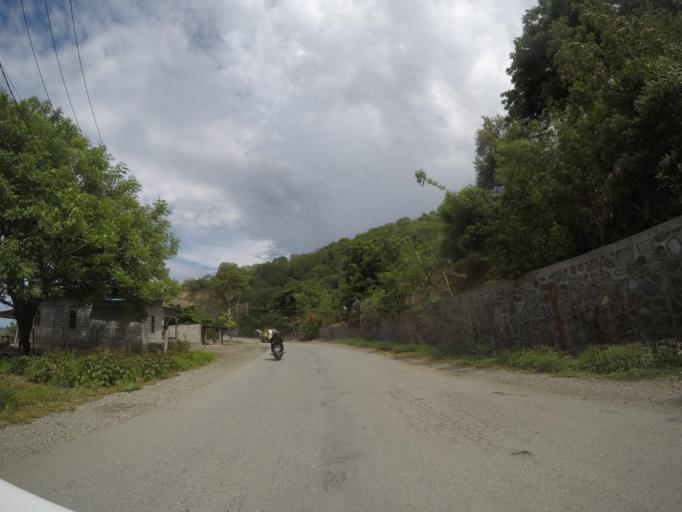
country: TL
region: Liquica
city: Maubara
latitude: -8.6270
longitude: 125.1601
